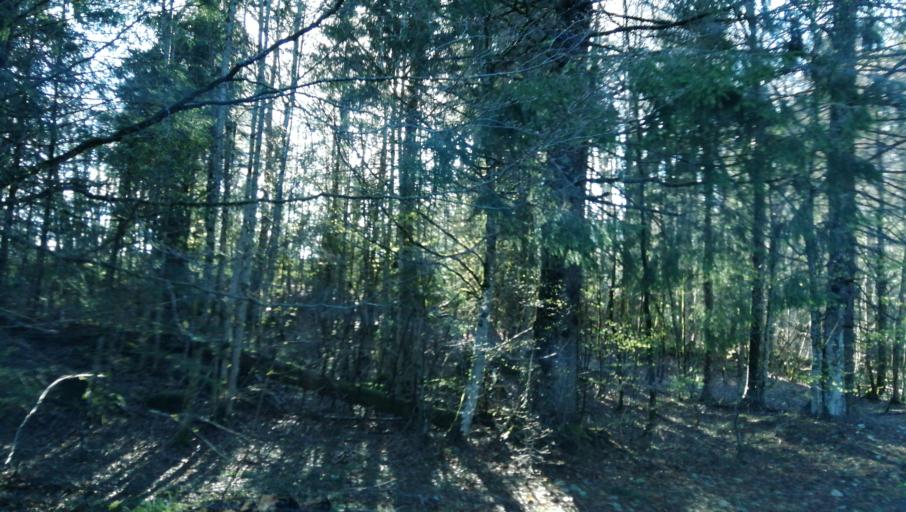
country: FR
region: Rhone-Alpes
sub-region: Departement de l'Ain
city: Chatillon-en-Michaille
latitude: 46.2612
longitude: 5.8081
